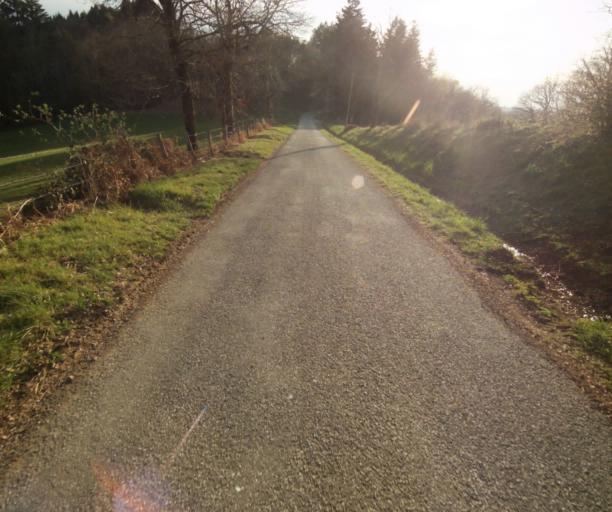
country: FR
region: Limousin
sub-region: Departement de la Correze
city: Correze
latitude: 45.3789
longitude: 1.8412
